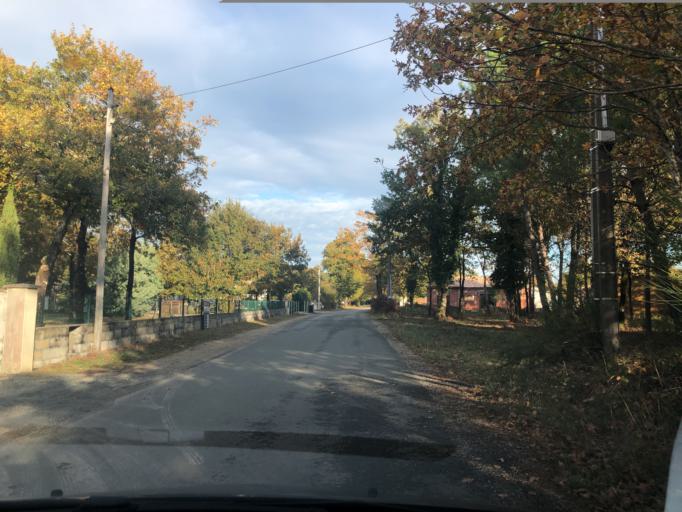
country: FR
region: Aquitaine
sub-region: Departement de la Gironde
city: Hourtin
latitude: 45.1834
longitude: -1.0513
